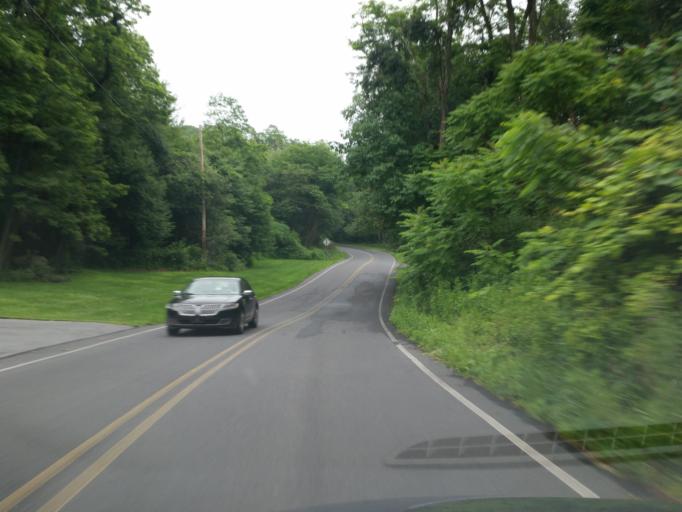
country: US
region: Pennsylvania
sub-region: Schuylkill County
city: Tremont
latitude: 40.5994
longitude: -76.4459
